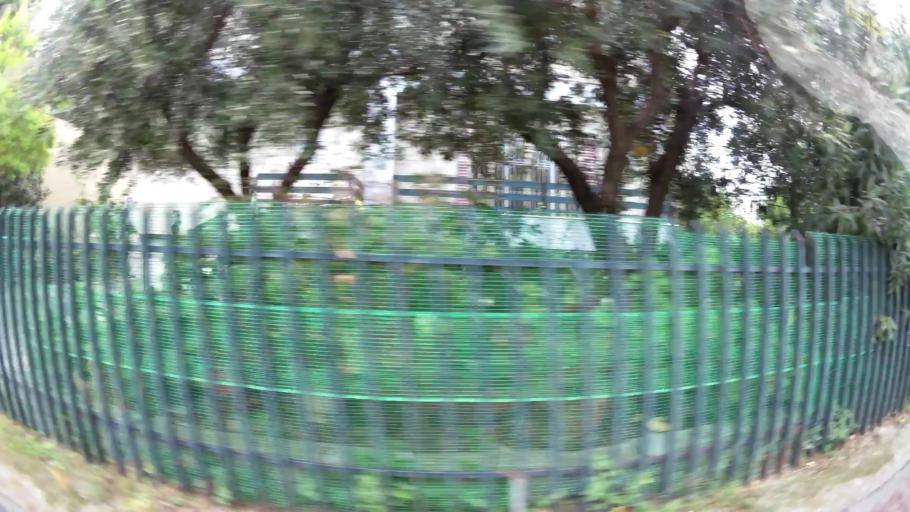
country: GR
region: Attica
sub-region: Nomarchia Athinas
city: Ilion
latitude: 38.0398
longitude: 23.7111
